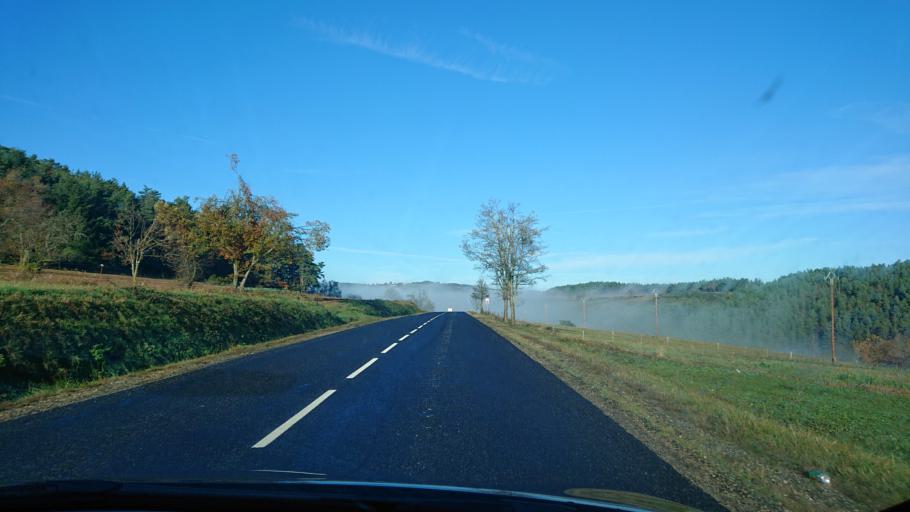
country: FR
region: Auvergne
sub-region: Departement de la Haute-Loire
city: Retournac
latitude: 45.2263
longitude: 4.0143
